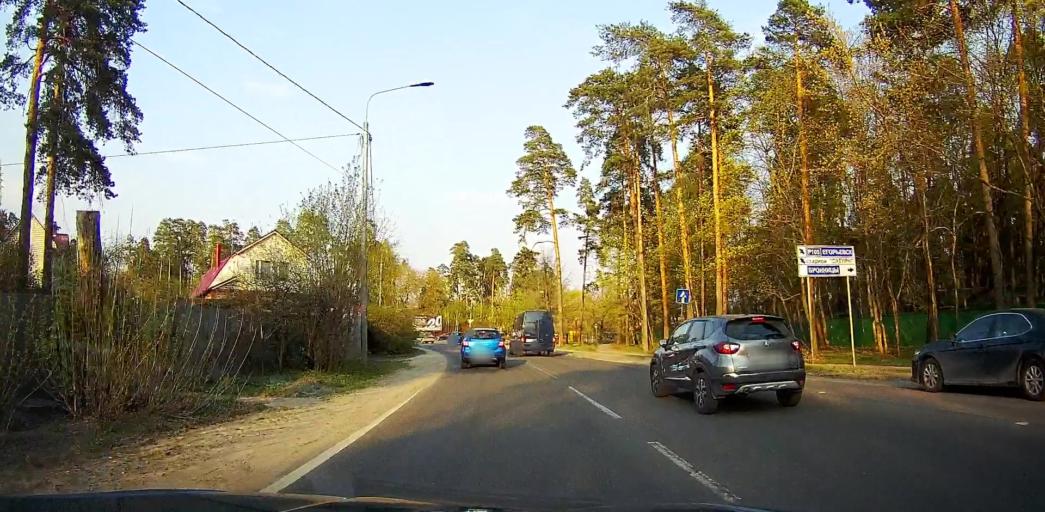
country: RU
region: Moskovskaya
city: Kratovo
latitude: 55.5711
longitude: 38.1826
